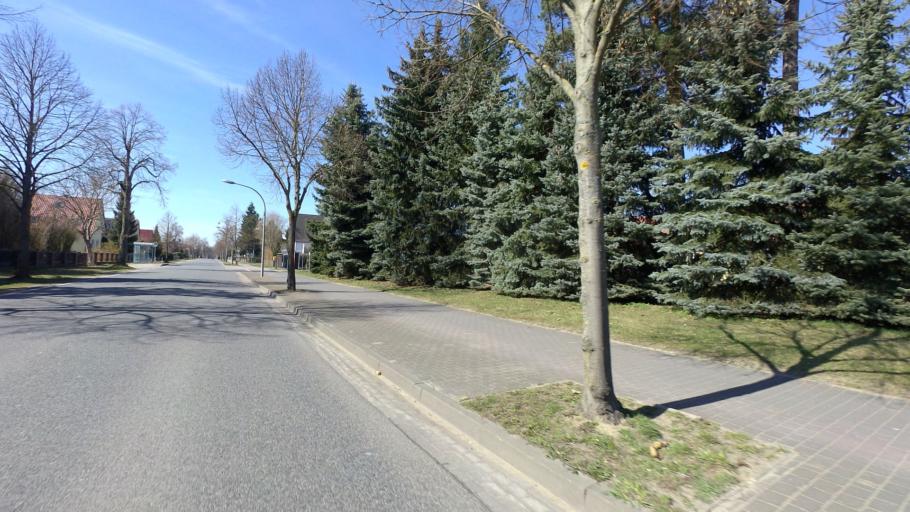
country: DE
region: Brandenburg
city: Muncheberg
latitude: 52.5075
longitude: 14.1322
